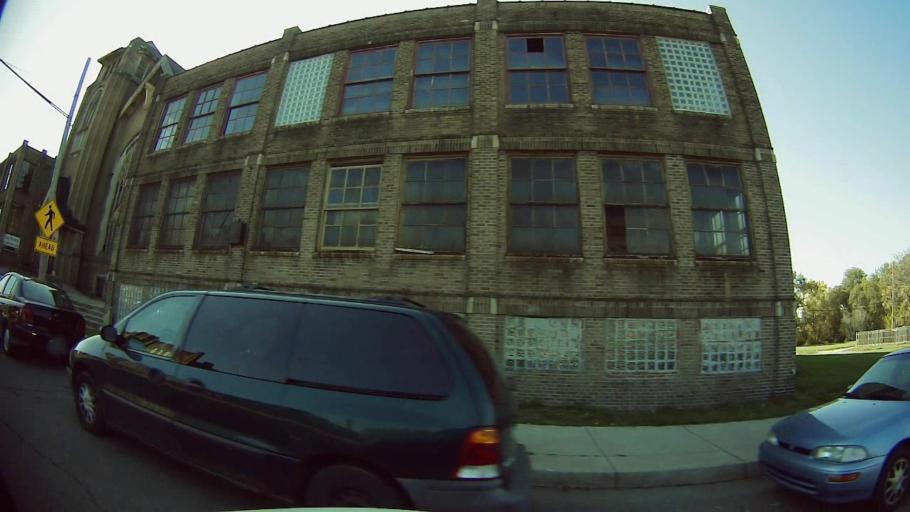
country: US
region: Michigan
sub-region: Wayne County
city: Highland Park
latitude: 42.3600
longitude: -83.0929
